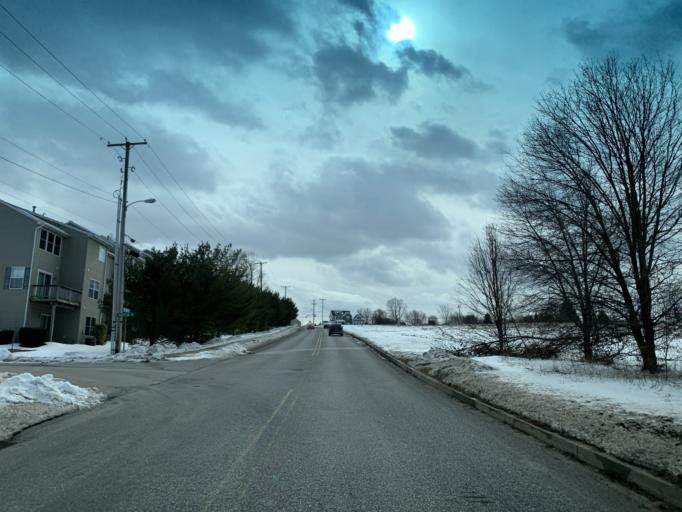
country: US
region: Pennsylvania
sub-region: York County
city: Shrewsbury
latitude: 39.7605
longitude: -76.6719
